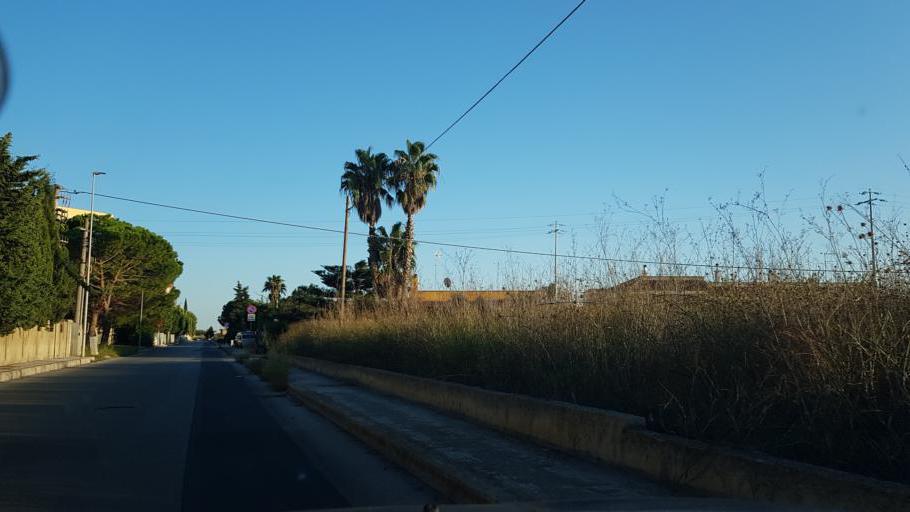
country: IT
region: Apulia
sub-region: Provincia di Brindisi
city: Brindisi
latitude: 40.6201
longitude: 17.9121
